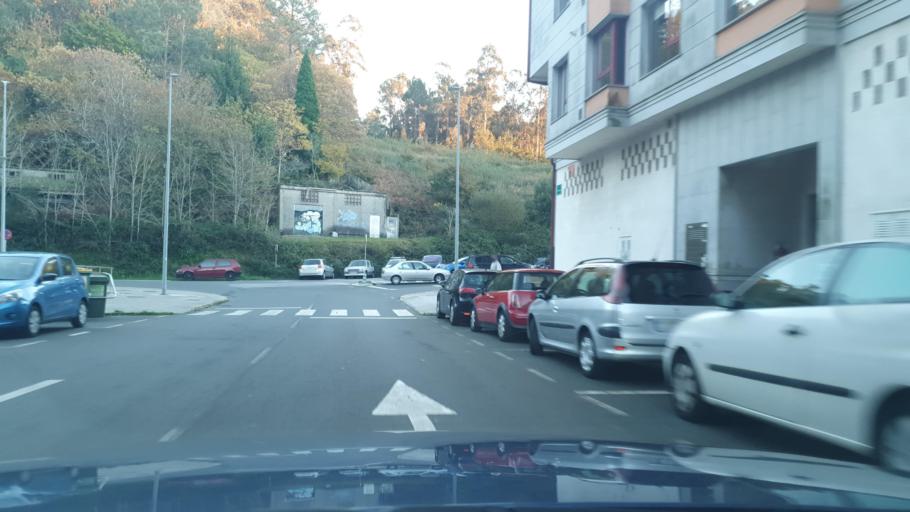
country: ES
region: Galicia
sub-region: Provincia da Coruna
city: Santiago de Compostela
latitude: 42.8442
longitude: -8.5753
